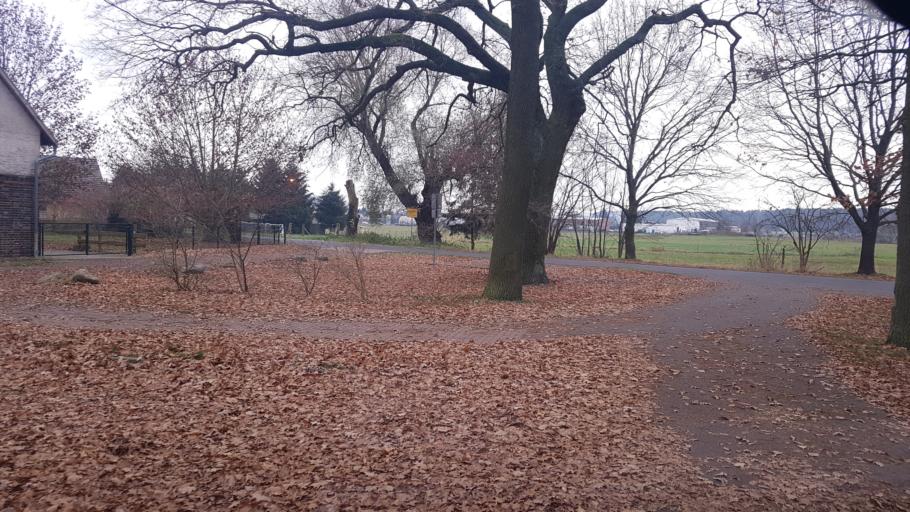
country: DE
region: Brandenburg
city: Schenkendobern
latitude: 51.9599
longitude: 14.6291
